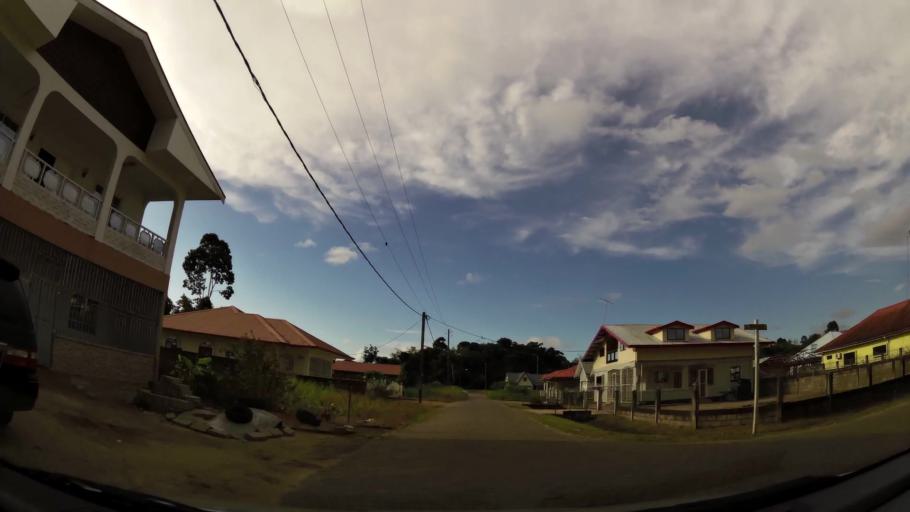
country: SR
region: Paramaribo
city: Paramaribo
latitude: 5.8491
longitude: -55.1781
